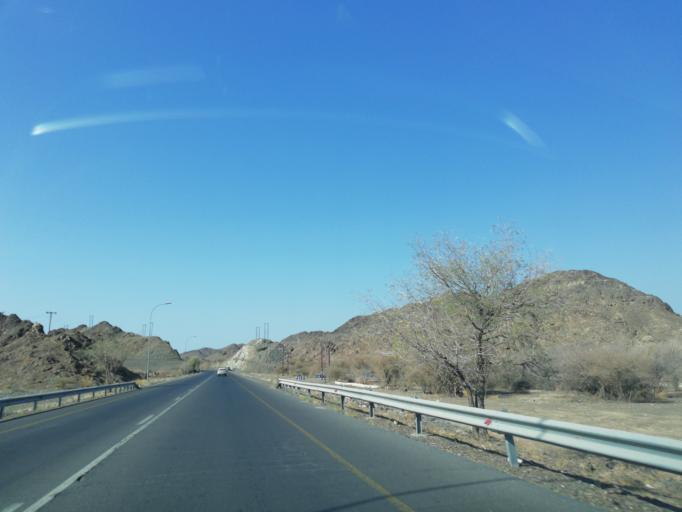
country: OM
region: Ash Sharqiyah
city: Ibra'
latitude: 22.8228
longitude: 58.1681
